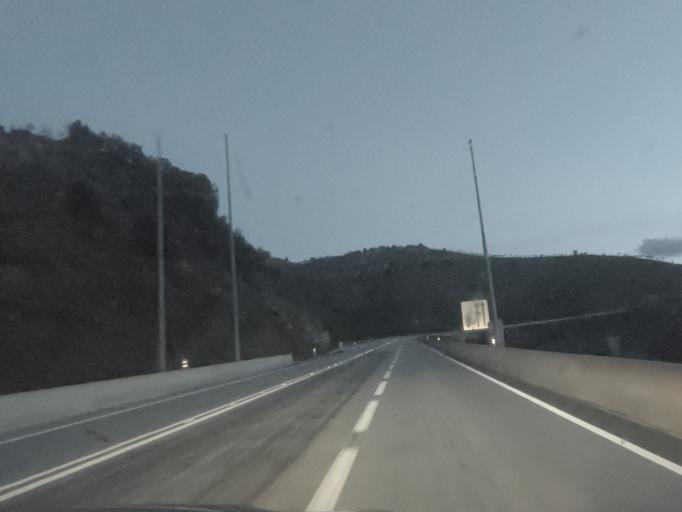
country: PT
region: Braganca
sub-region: Alfandega da Fe
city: Alfandega da Fe
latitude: 41.2831
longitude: -6.8707
